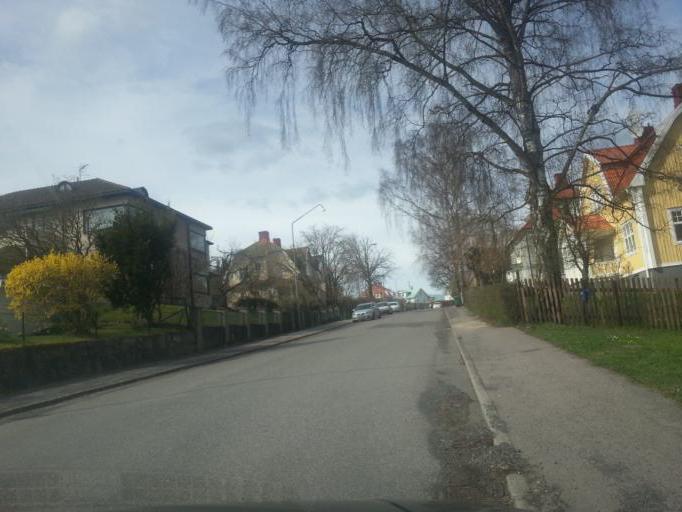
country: SE
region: Joenkoeping
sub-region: Jonkopings Kommun
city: Jonkoping
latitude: 57.7848
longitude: 14.1464
